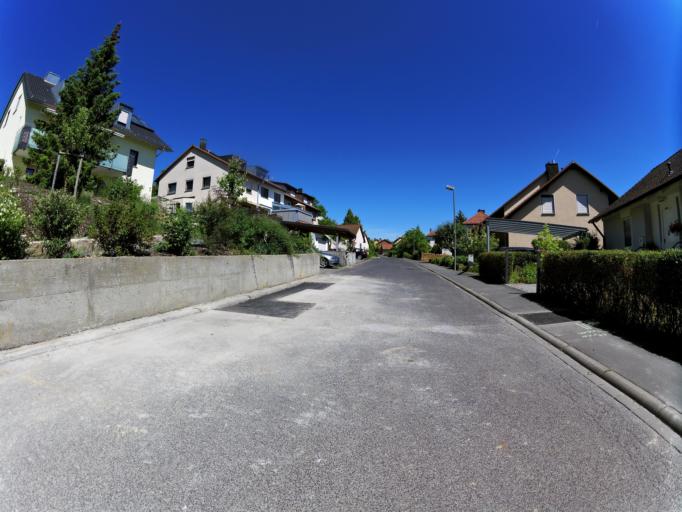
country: DE
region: Bavaria
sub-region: Regierungsbezirk Unterfranken
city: Ochsenfurt
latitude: 49.6734
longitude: 10.0548
